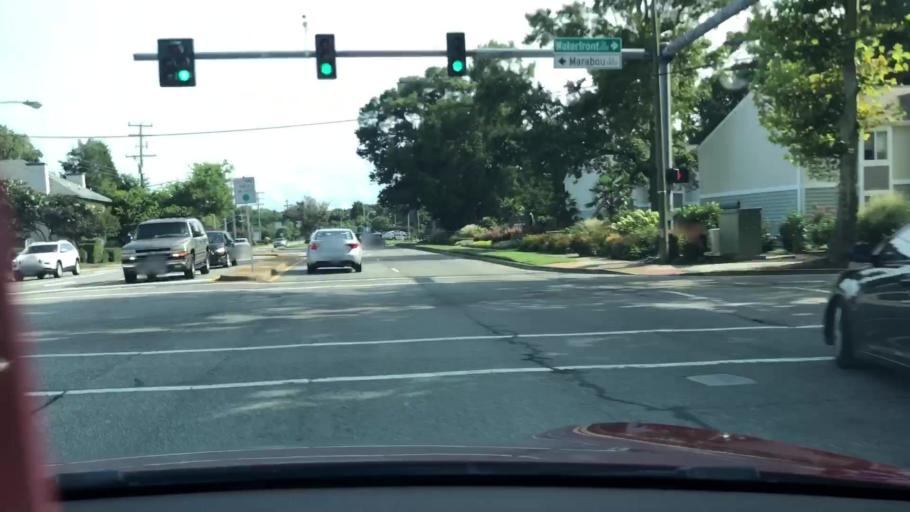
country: US
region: Virginia
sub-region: City of Virginia Beach
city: Virginia Beach
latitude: 36.8505
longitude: -75.9944
